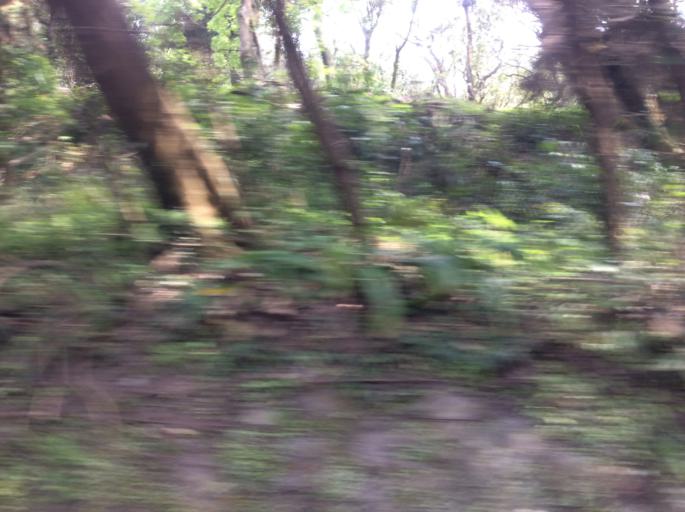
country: TW
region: Taipei
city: Taipei
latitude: 25.1522
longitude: 121.5455
